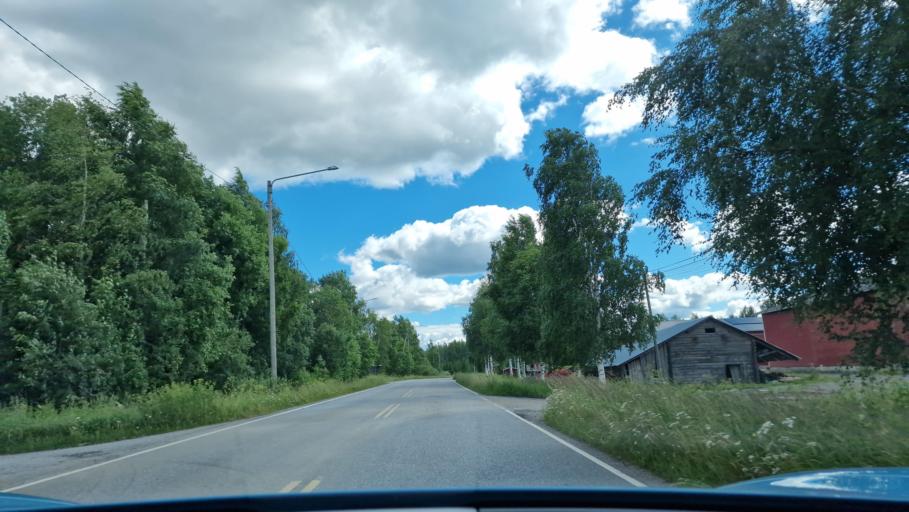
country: FI
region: Southern Ostrobothnia
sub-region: Jaerviseutu
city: Soini
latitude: 62.8432
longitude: 24.3269
